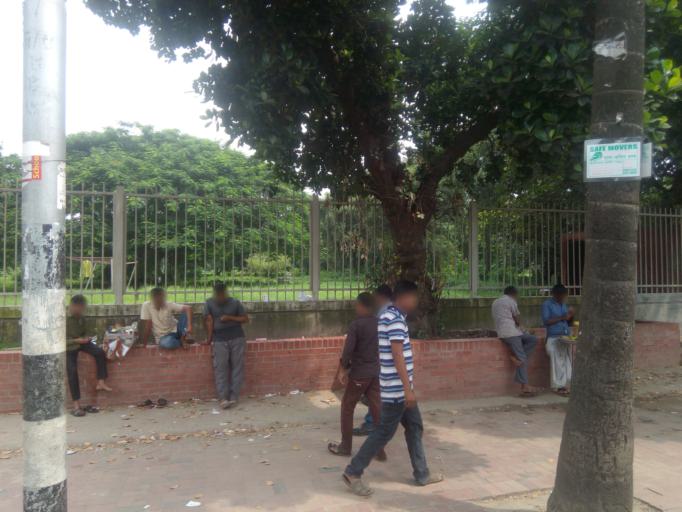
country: BD
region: Dhaka
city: Azimpur
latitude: 23.7586
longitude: 90.3747
